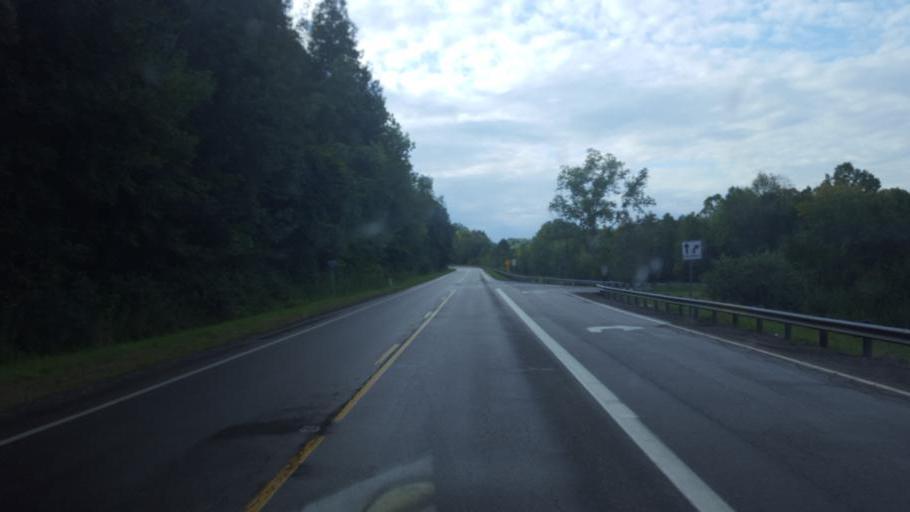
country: US
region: Ohio
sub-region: Holmes County
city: Millersburg
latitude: 40.5023
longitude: -81.9621
